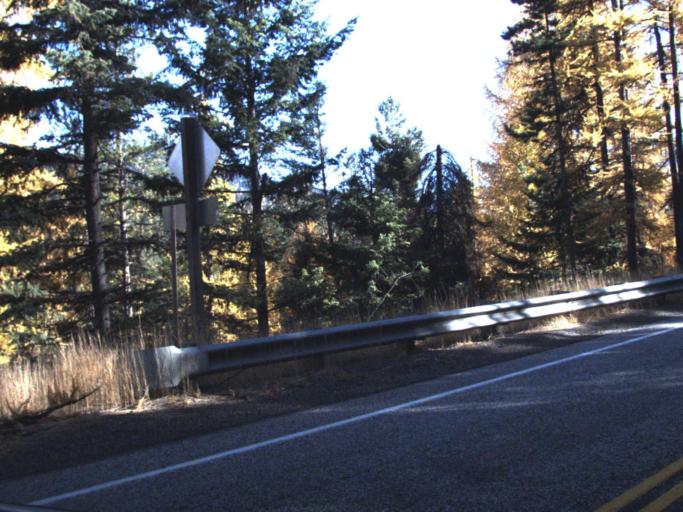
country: US
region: Washington
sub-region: Ferry County
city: Republic
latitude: 48.6107
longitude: -118.5427
